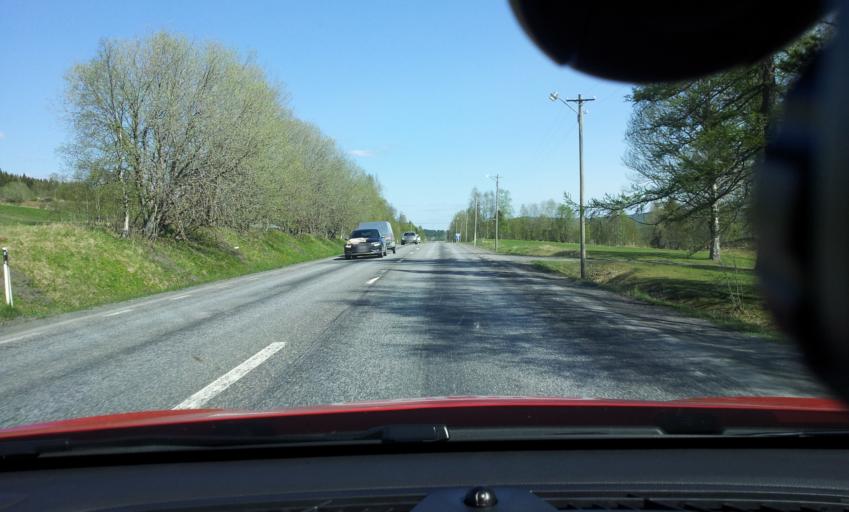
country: SE
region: Jaemtland
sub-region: Are Kommun
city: Jarpen
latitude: 63.3132
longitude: 13.3033
